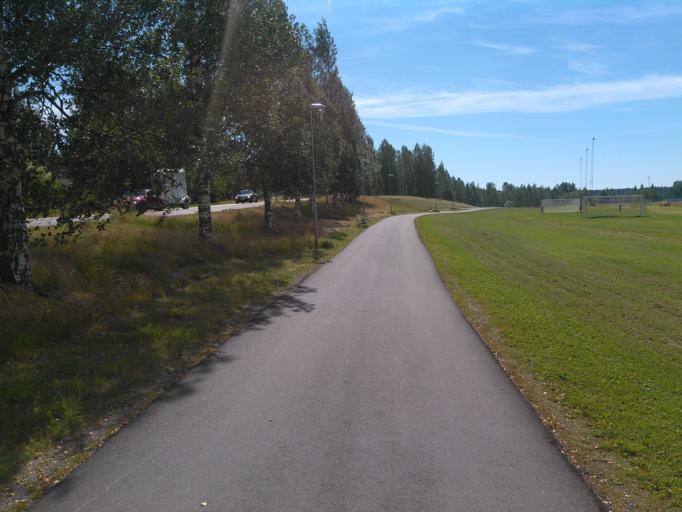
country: SE
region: Vaesterbotten
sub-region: Umea Kommun
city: Ersmark
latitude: 63.8415
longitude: 20.3162
